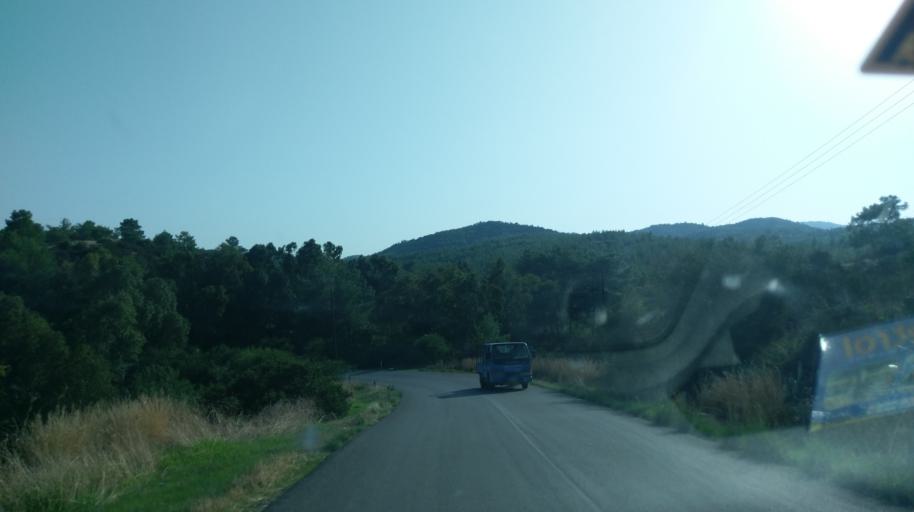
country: CY
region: Lefkosia
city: Kato Pyrgos
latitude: 35.1573
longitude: 32.7588
